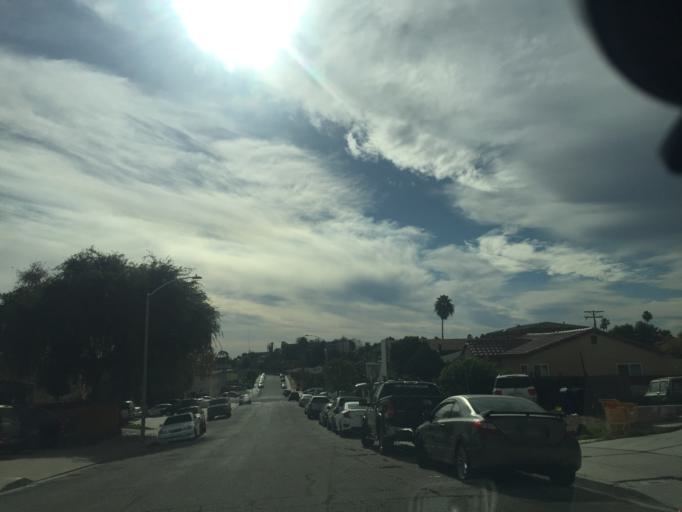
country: US
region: California
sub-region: San Diego County
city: Lemon Grove
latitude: 32.7543
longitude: -117.0858
